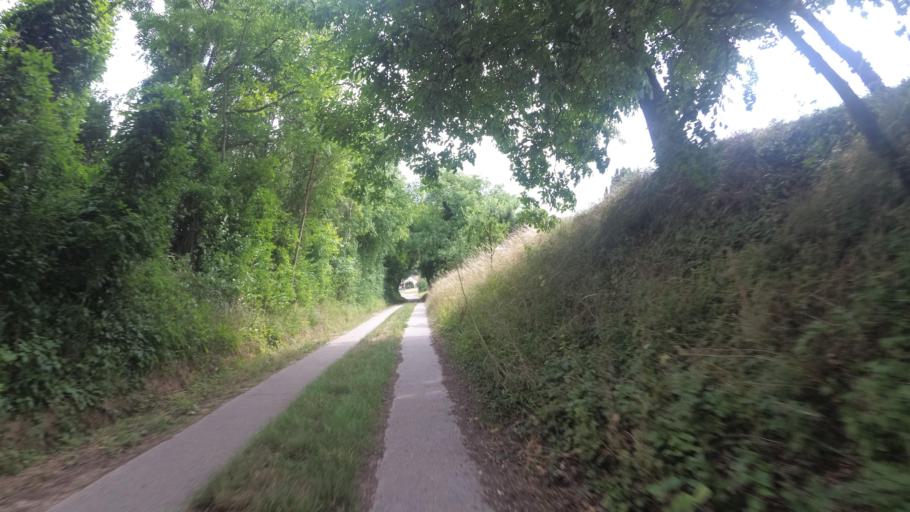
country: DE
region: Baden-Wuerttemberg
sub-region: Regierungsbezirk Stuttgart
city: Oedheim
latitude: 49.2463
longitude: 9.2270
